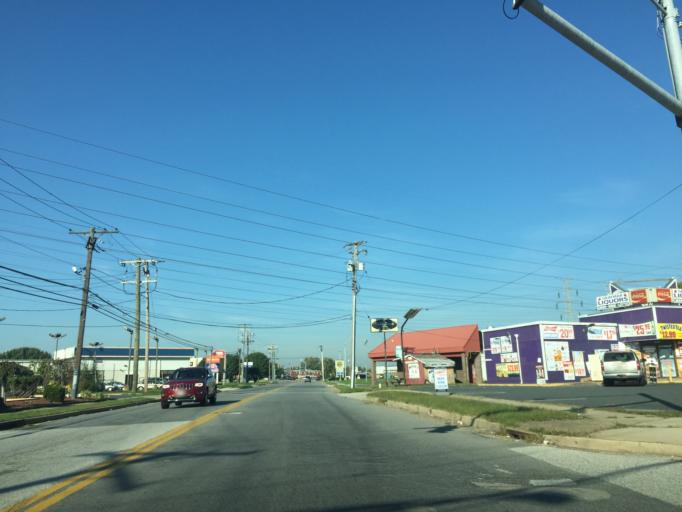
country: US
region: Maryland
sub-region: Baltimore County
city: Dundalk
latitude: 39.2799
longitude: -76.5019
